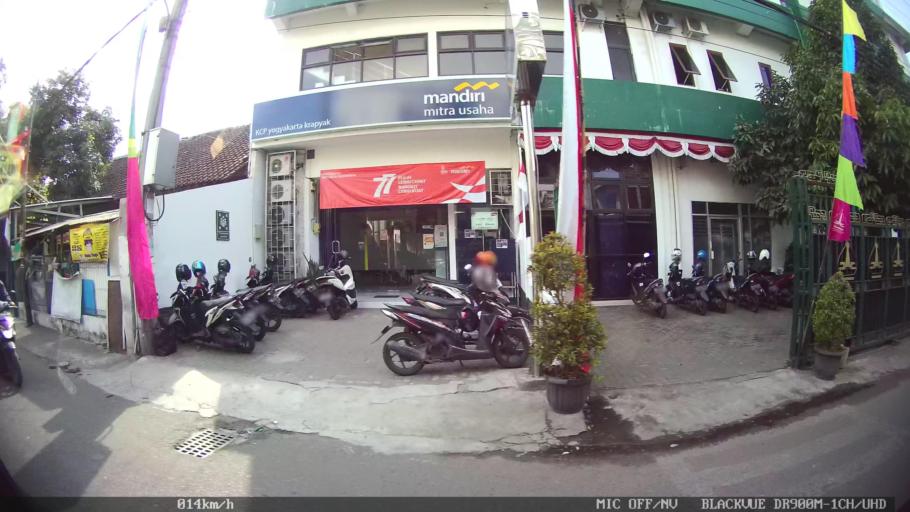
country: ID
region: Daerah Istimewa Yogyakarta
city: Kasihan
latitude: -7.8256
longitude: 110.3614
